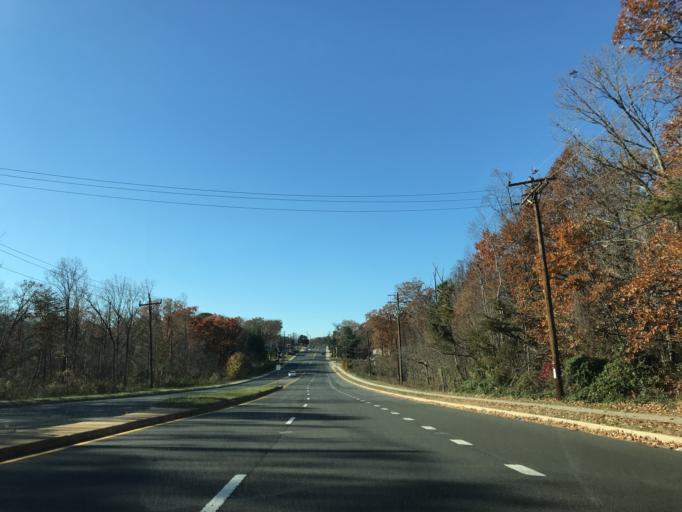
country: US
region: Maryland
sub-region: Prince George's County
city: Calverton
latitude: 39.0467
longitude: -76.9386
